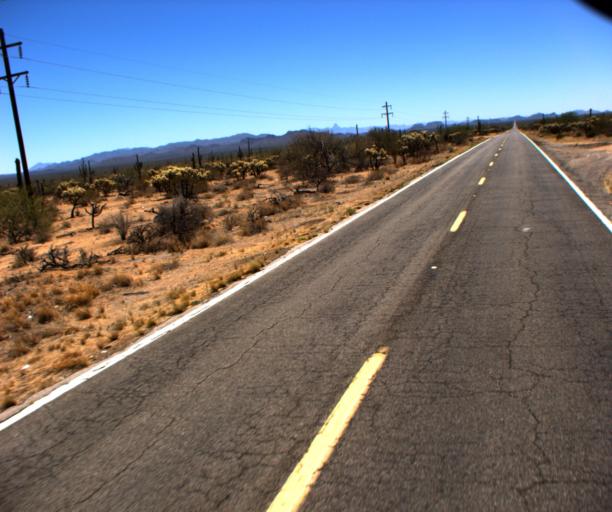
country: US
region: Arizona
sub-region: Pima County
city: Sells
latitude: 32.1104
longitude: -112.0738
